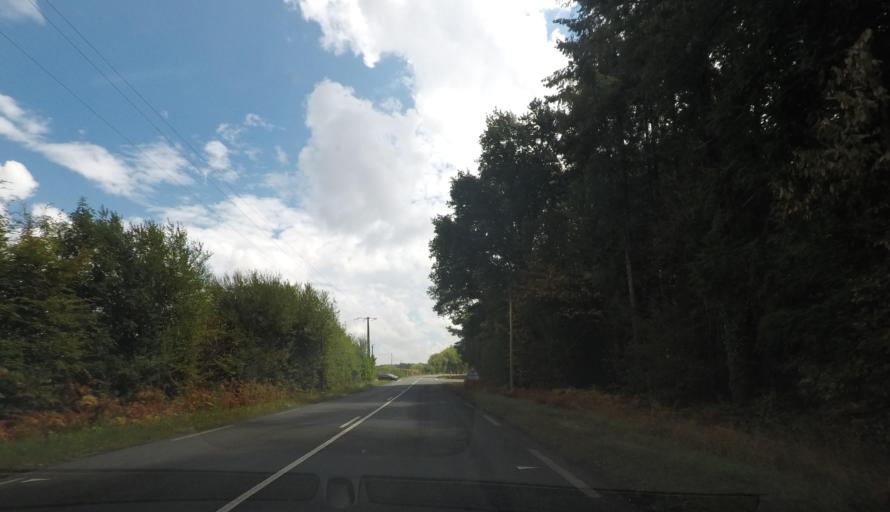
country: FR
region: Pays de la Loire
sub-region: Departement de la Sarthe
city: Saint-Cosme-en-Vairais
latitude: 48.2609
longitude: 0.5331
